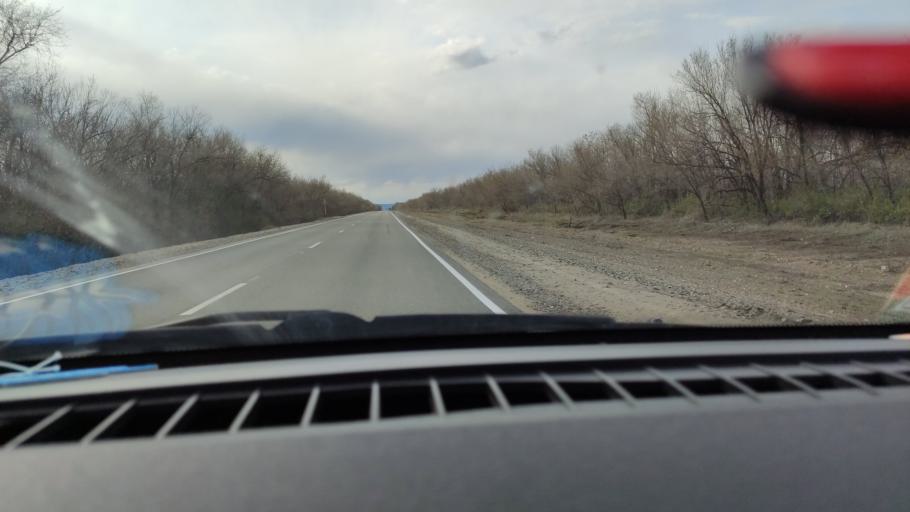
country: RU
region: Saratov
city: Privolzhskiy
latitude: 51.1702
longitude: 45.9391
